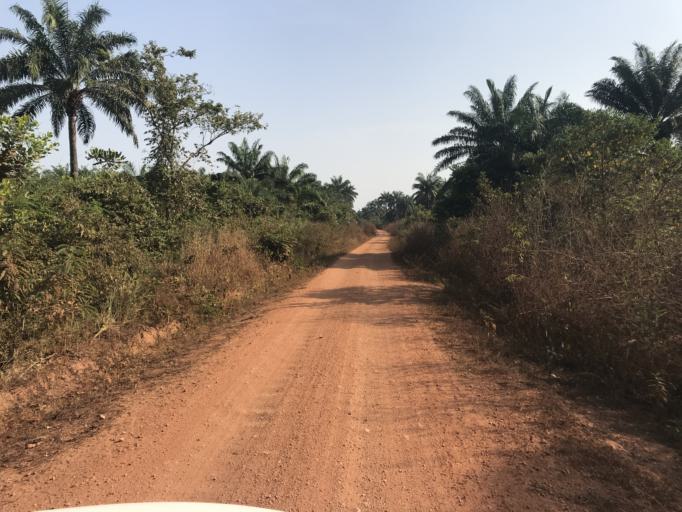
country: NG
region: Osun
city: Inisa
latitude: 7.7903
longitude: 4.2967
